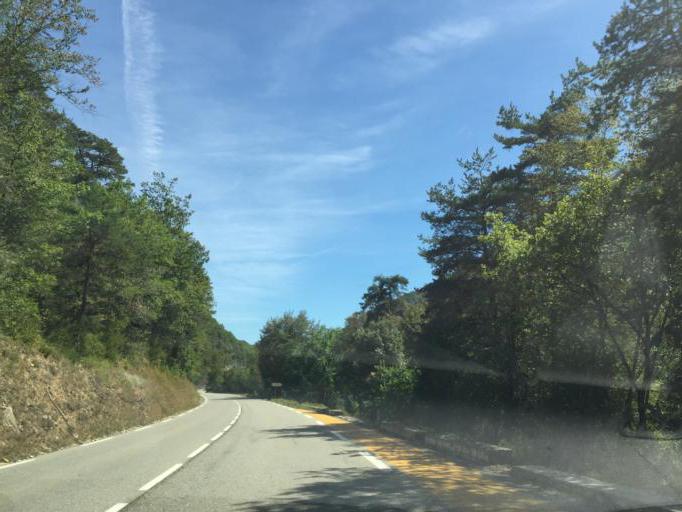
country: FR
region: Provence-Alpes-Cote d'Azur
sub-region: Departement des Alpes-Maritimes
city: Gilette
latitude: 43.9856
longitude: 7.1366
